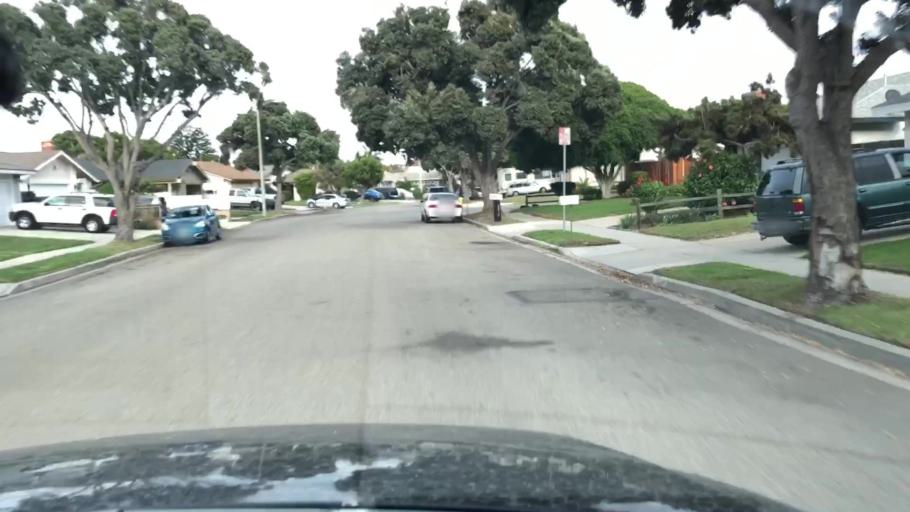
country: US
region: California
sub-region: Ventura County
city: Oxnard Shores
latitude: 34.1883
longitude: -119.2169
